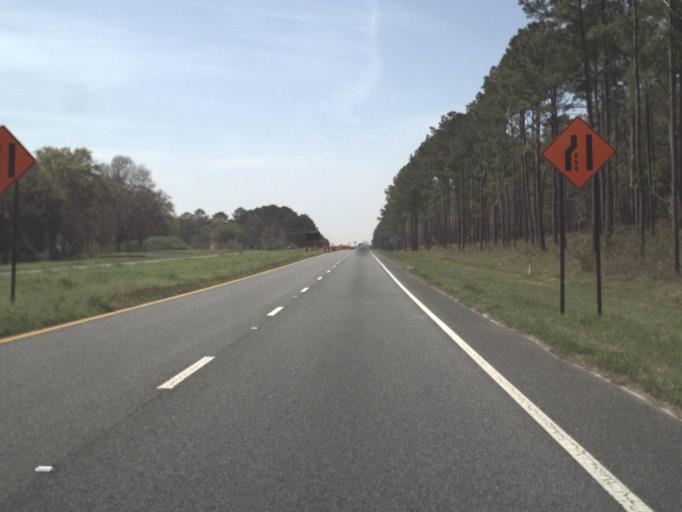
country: US
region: Florida
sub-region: Gadsden County
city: Midway
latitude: 30.5524
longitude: -84.4972
